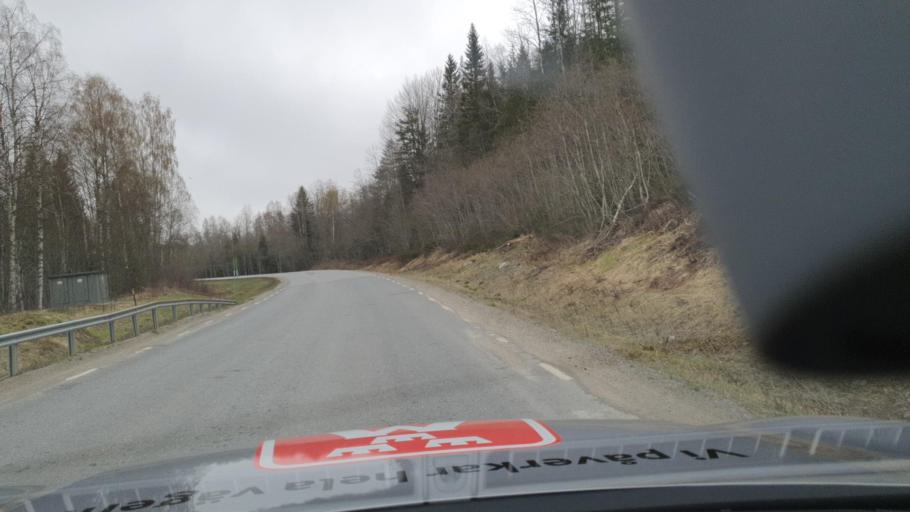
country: SE
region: Vaesternorrland
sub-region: OErnskoeldsviks Kommun
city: Husum
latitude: 63.5671
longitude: 19.0421
